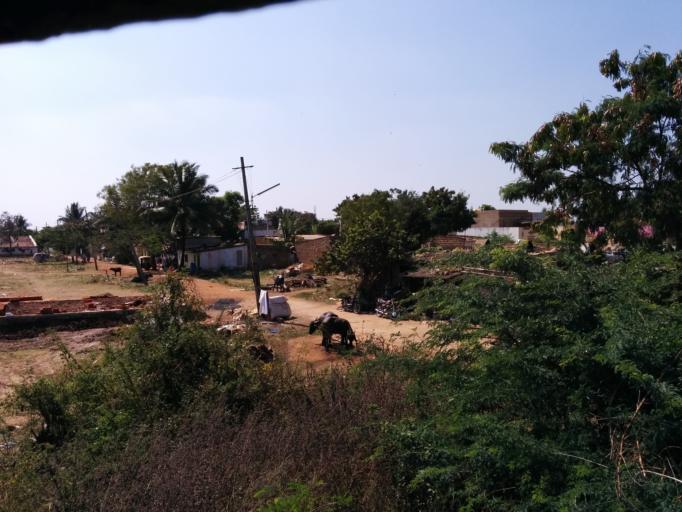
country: IN
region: Karnataka
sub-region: Dharwad
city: Hubli
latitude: 15.3902
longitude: 75.1159
